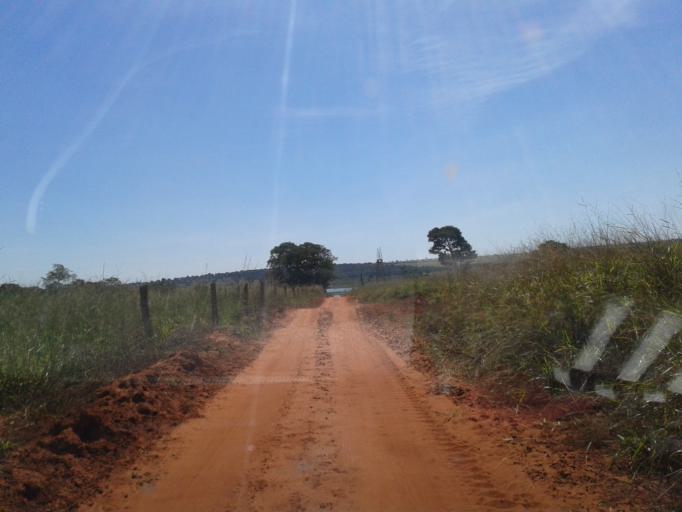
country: BR
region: Minas Gerais
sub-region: Santa Vitoria
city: Santa Vitoria
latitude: -19.0113
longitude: -50.3256
